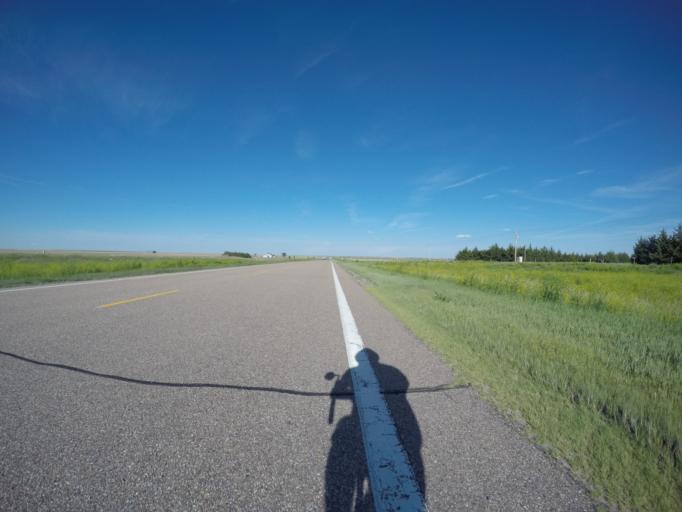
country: US
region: Kansas
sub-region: Cheyenne County
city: Saint Francis
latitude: 39.7569
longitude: -101.9066
